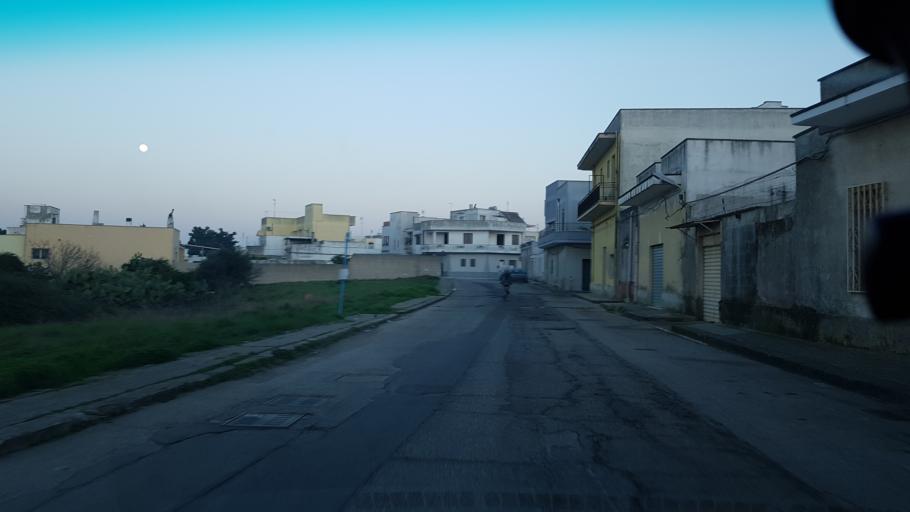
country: IT
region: Apulia
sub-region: Provincia di Brindisi
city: Mesagne
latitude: 40.5635
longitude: 17.7966
